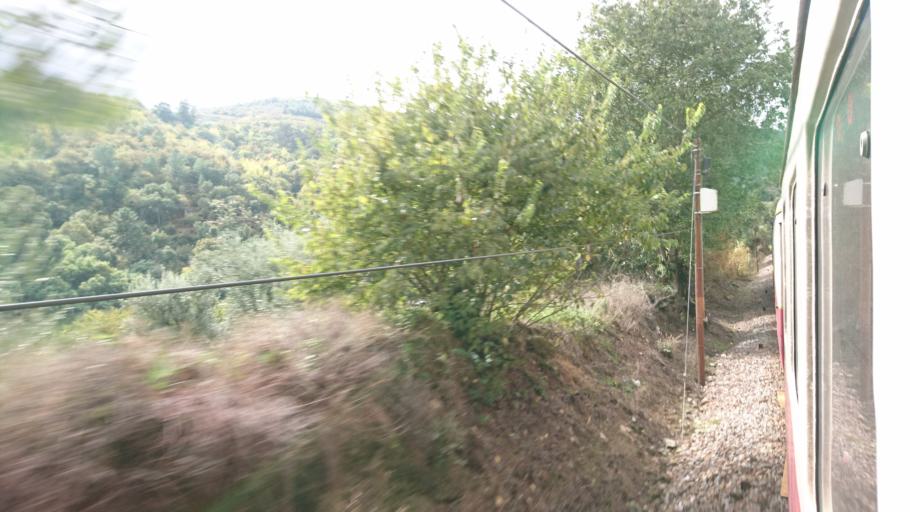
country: PT
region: Viseu
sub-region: Resende
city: Resende
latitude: 41.1206
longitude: -7.9244
